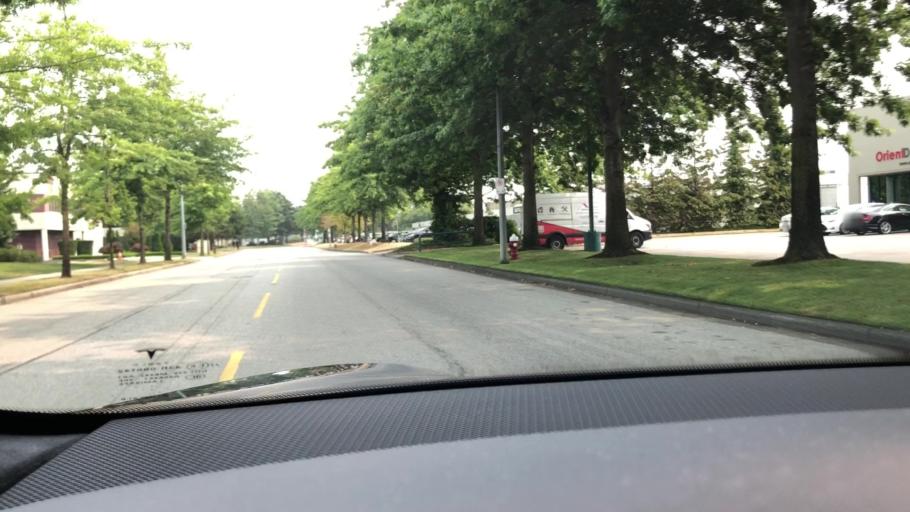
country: CA
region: British Columbia
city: Ladner
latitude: 49.1308
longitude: -123.0993
